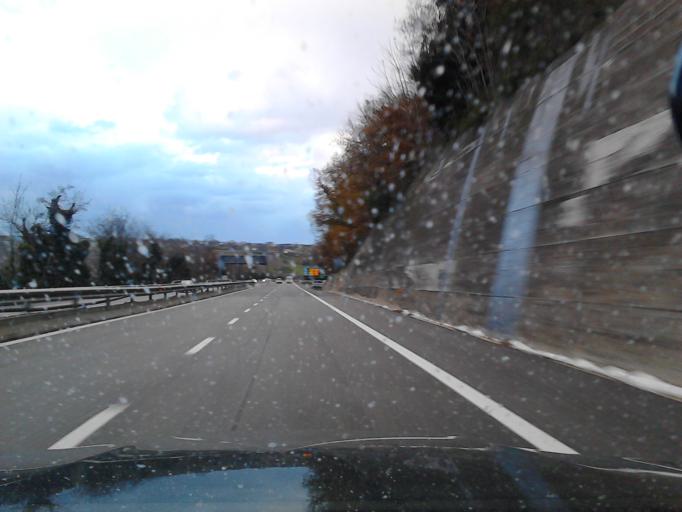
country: IT
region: Abruzzo
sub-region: Provincia di Chieti
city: San Vito Chietino
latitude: 42.2768
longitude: 14.4354
